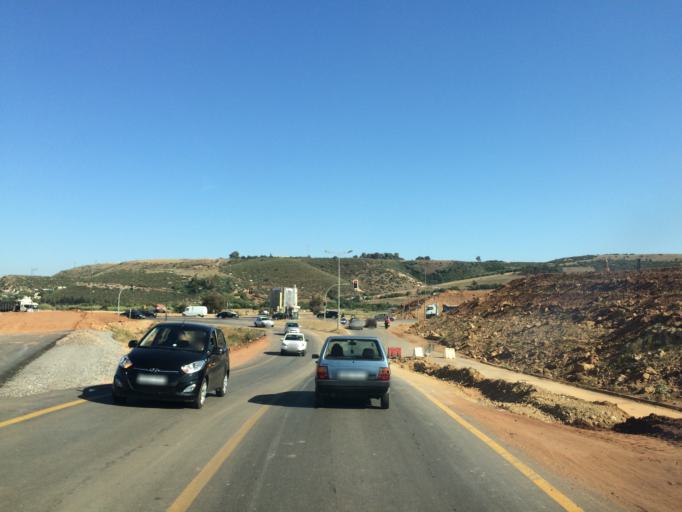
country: MA
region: Rabat-Sale-Zemmour-Zaer
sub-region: Rabat
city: Rabat
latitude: 33.9875
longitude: -6.7910
